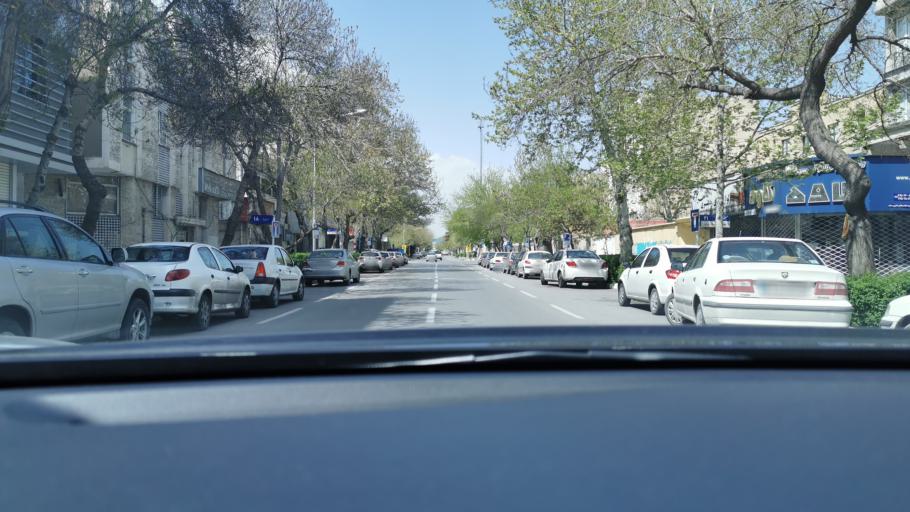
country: IR
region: Razavi Khorasan
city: Mashhad
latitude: 36.2982
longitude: 59.5923
